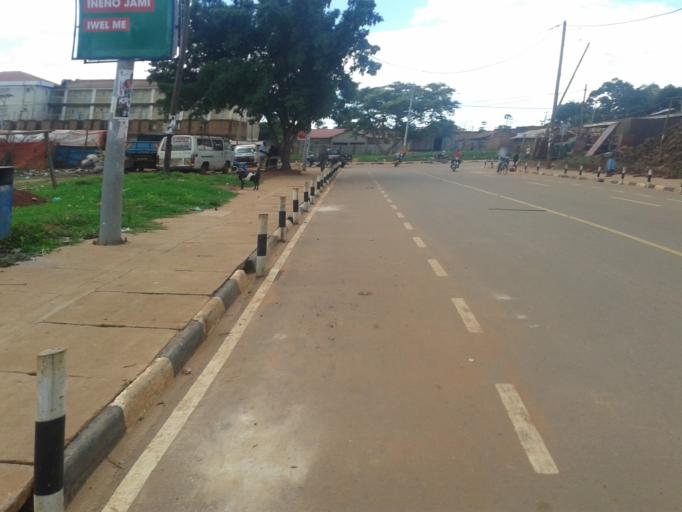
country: UG
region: Northern Region
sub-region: Gulu District
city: Gulu
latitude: 2.7694
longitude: 32.3010
